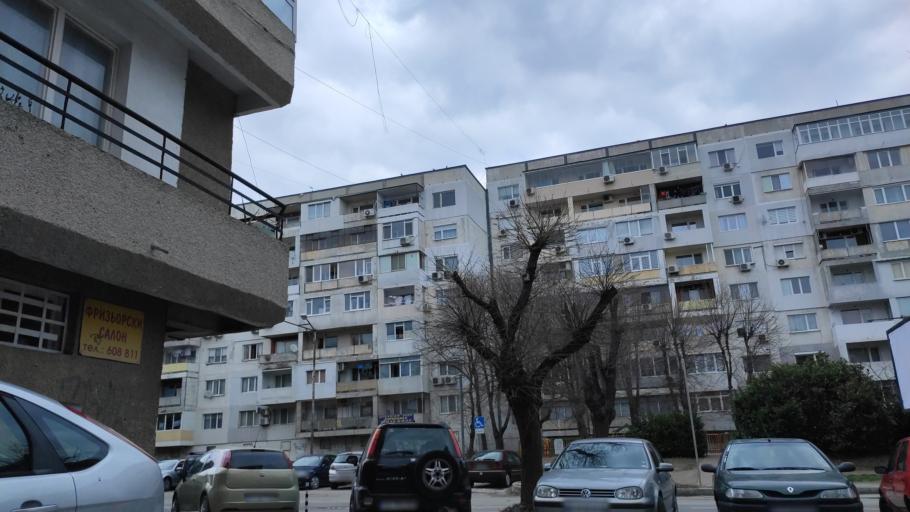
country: BG
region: Varna
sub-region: Obshtina Varna
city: Varna
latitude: 43.2153
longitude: 27.9200
